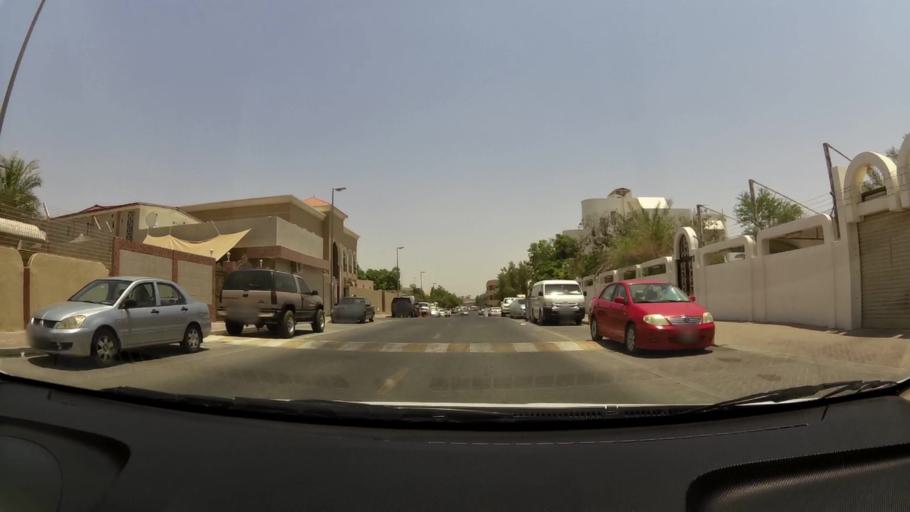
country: AE
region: Ash Shariqah
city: Sharjah
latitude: 25.2873
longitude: 55.3320
